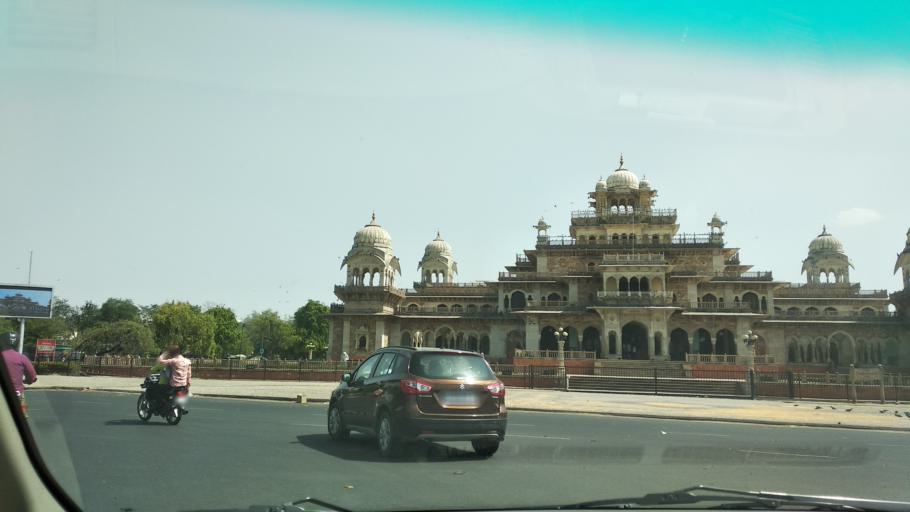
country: IN
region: Rajasthan
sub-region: Jaipur
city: Jaipur
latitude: 26.9125
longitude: 75.8198
